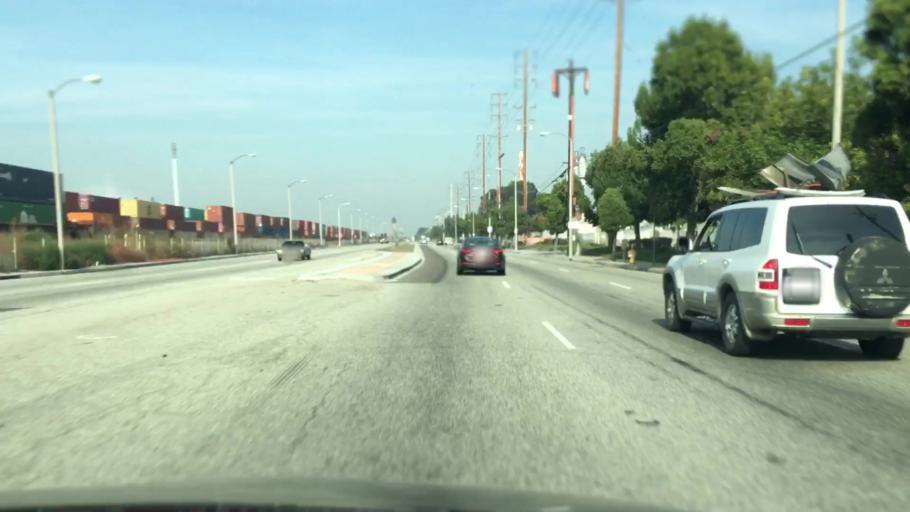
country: US
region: California
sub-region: Los Angeles County
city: Carson
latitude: 33.8095
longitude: -118.2340
